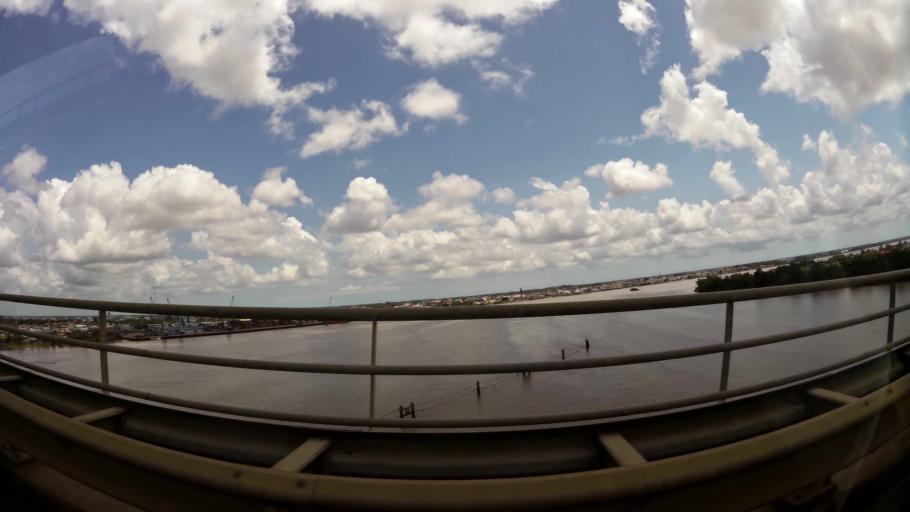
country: SR
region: Paramaribo
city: Paramaribo
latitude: 5.8059
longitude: -55.1614
